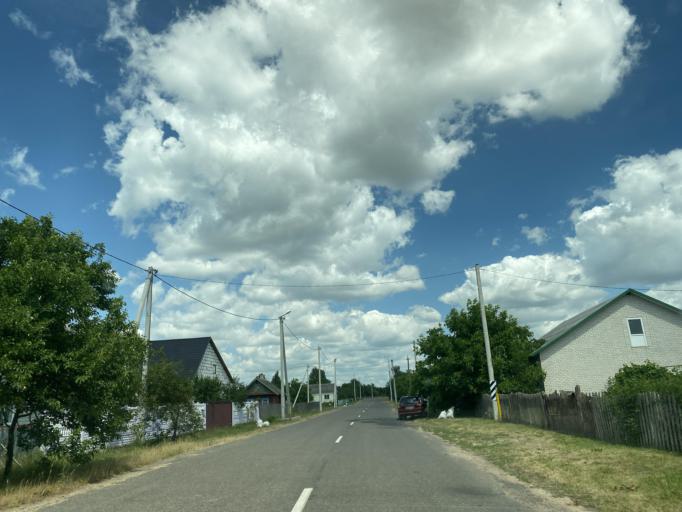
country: BY
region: Brest
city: Ivanava
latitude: 52.1694
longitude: 25.5595
